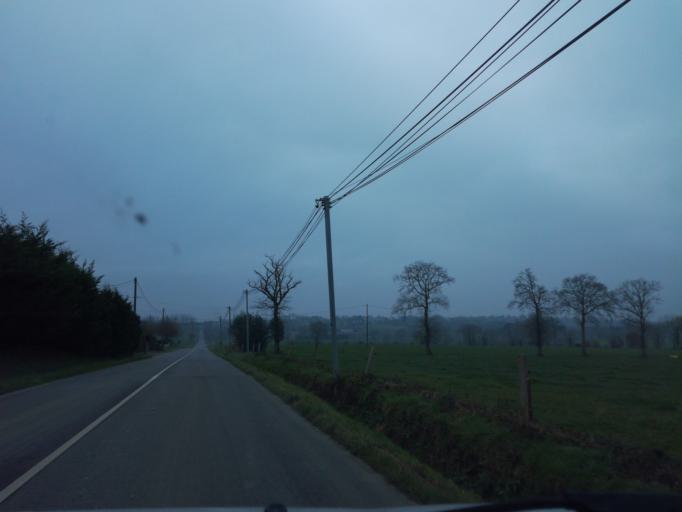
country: FR
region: Brittany
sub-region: Departement d'Ille-et-Vilaine
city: Gosne
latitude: 48.2583
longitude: -1.4526
